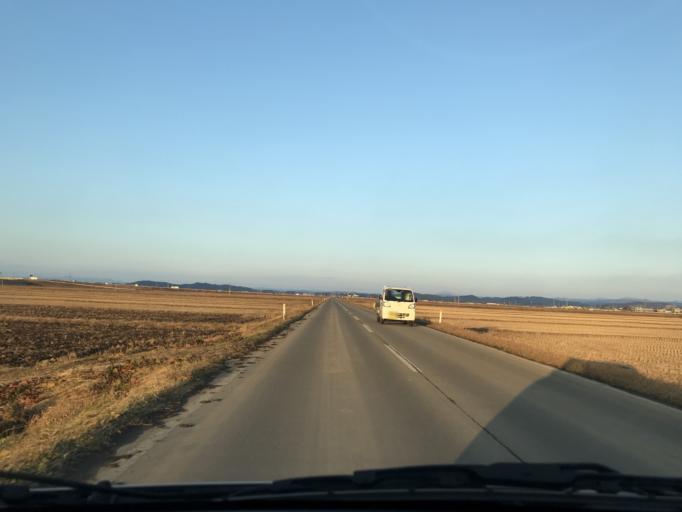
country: JP
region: Miyagi
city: Wakuya
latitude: 38.7118
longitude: 141.1548
